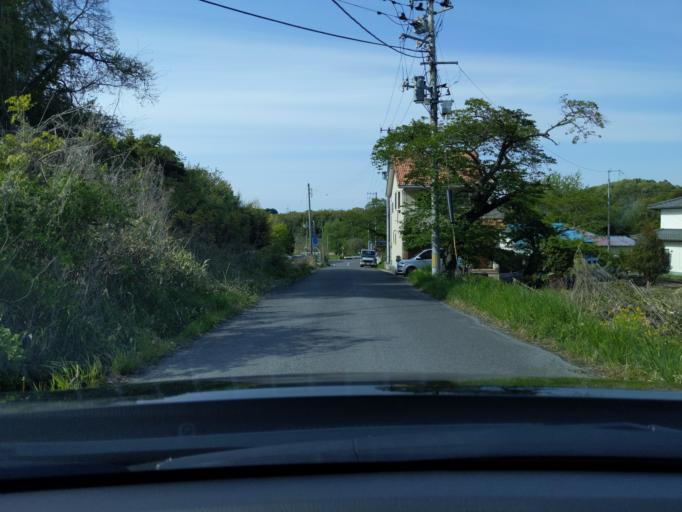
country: JP
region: Fukushima
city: Sukagawa
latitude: 37.3140
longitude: 140.4312
